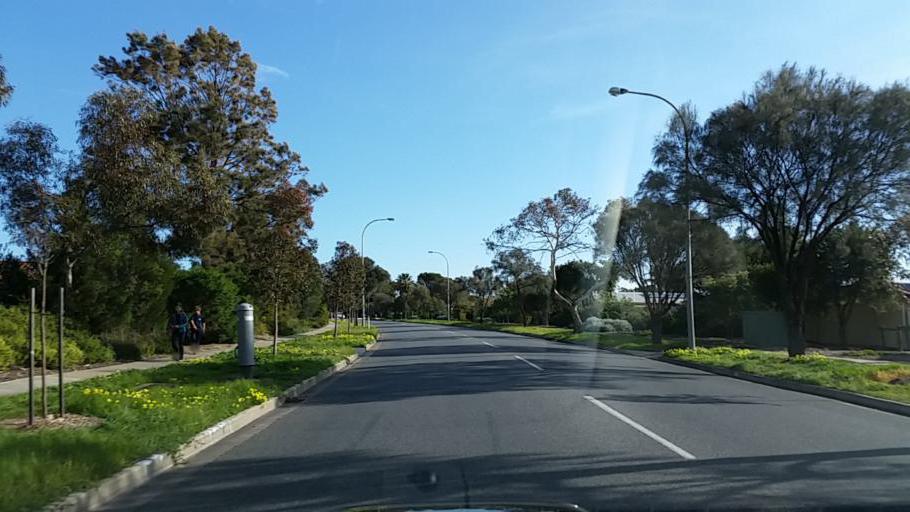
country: AU
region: South Australia
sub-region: Charles Sturt
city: West Lakes Shore
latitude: -34.8616
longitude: 138.4880
